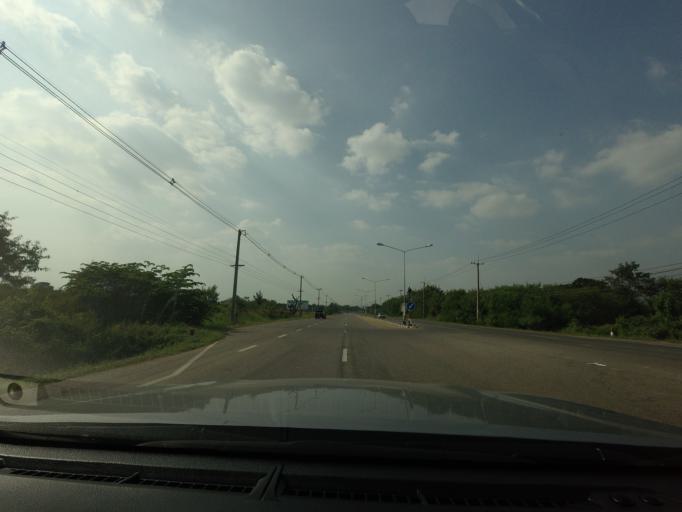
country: TH
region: Sukhothai
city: Sukhothai
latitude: 17.0239
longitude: 99.8923
